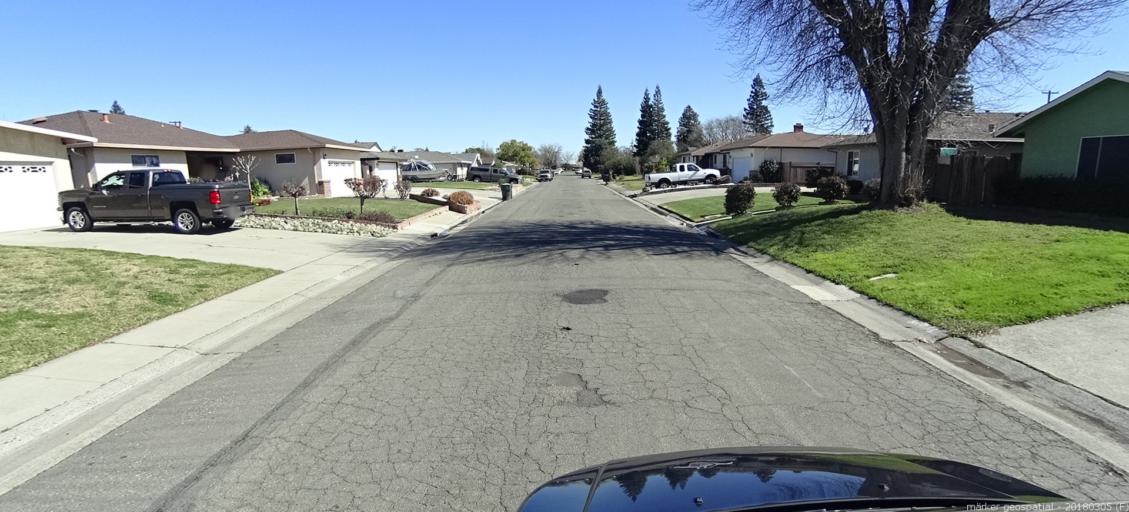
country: US
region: California
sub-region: Sacramento County
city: Florin
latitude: 38.4991
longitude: -121.4135
